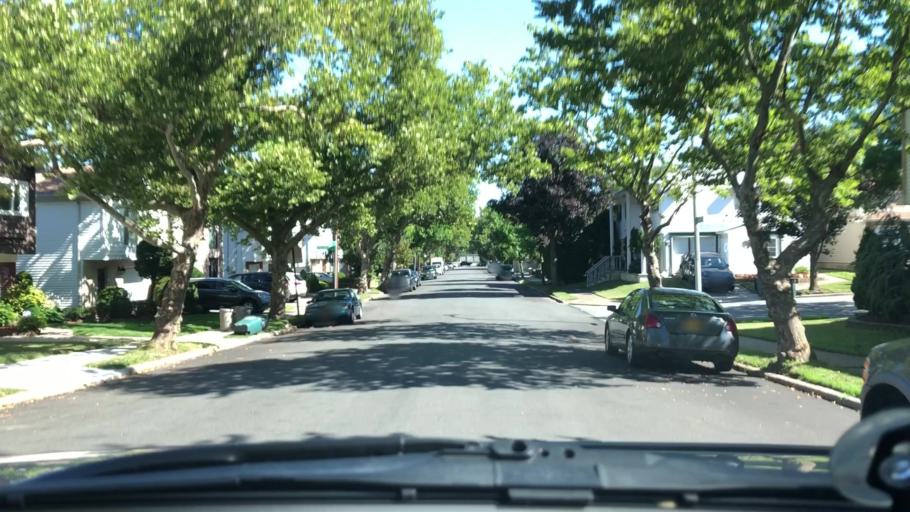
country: US
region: New York
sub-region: Richmond County
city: Staten Island
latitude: 40.6037
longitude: -74.1378
